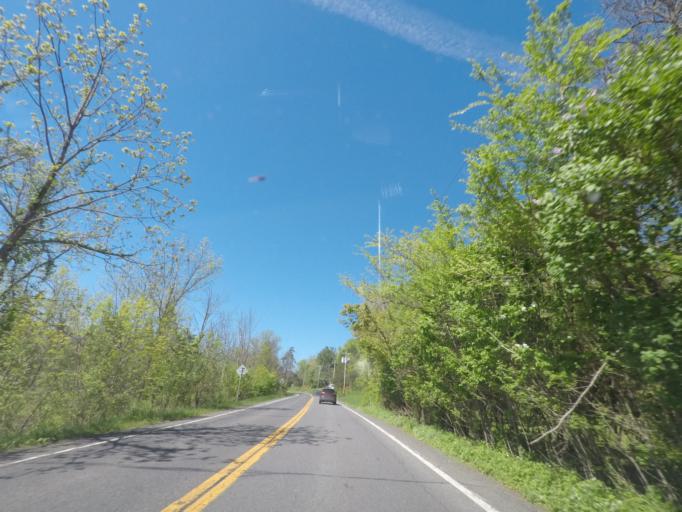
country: US
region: New York
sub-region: Ulster County
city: Saugerties
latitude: 42.1182
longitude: -73.9342
